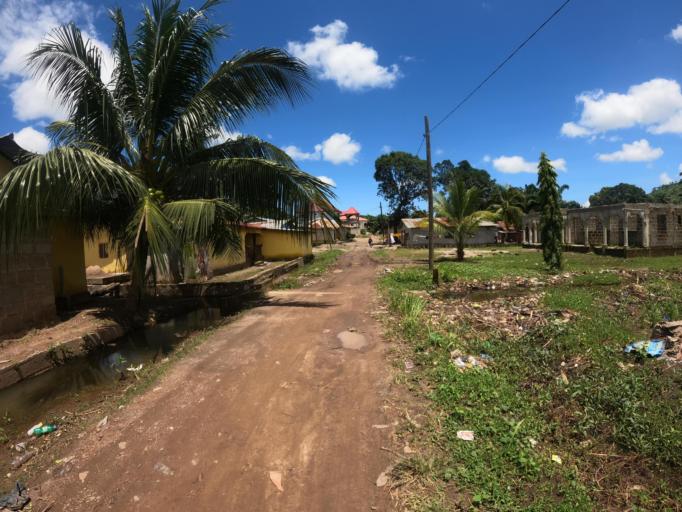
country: SL
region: Northern Province
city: Makeni
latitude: 8.8956
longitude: -12.0605
